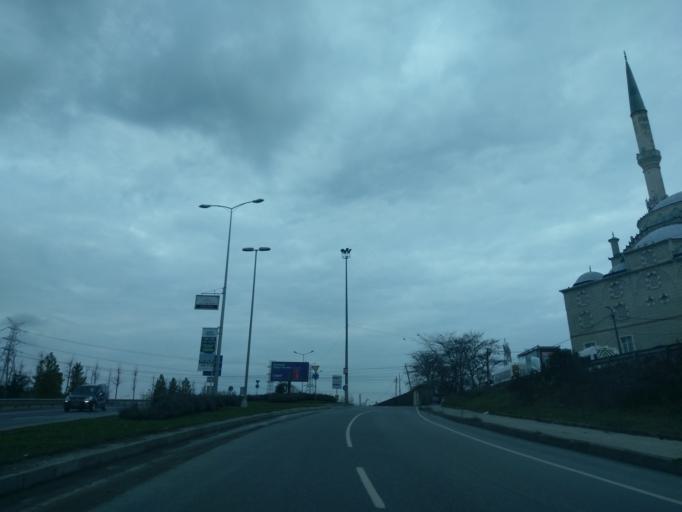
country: TR
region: Istanbul
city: Sisli
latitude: 41.1007
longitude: 28.9633
